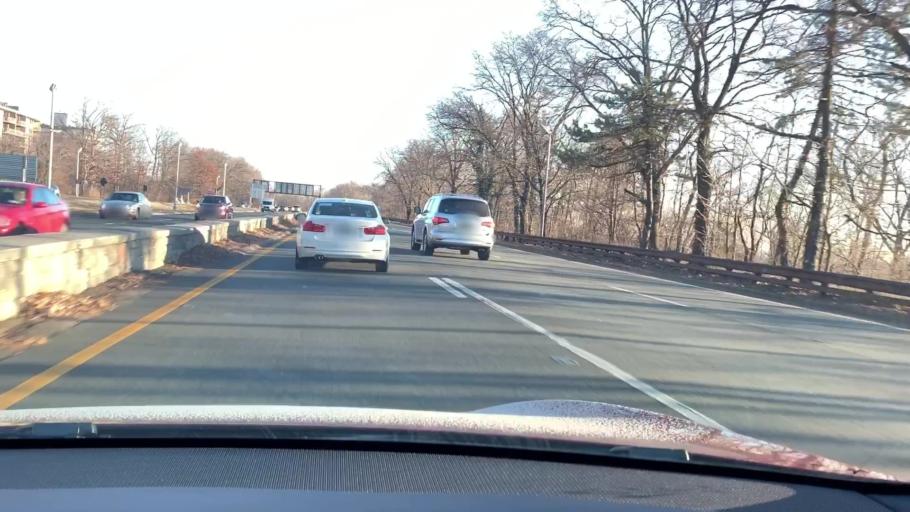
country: US
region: New Jersey
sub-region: Bergen County
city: Fort Lee
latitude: 40.8606
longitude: -73.9587
